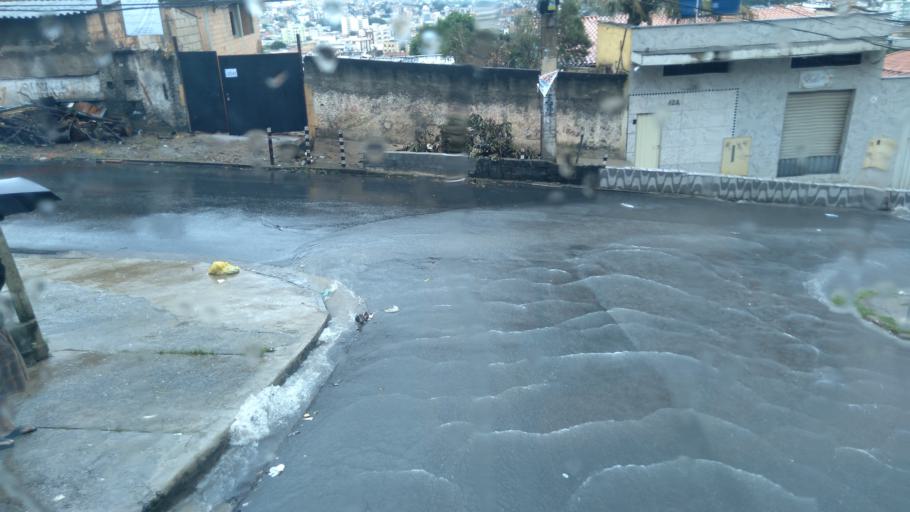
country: BR
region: Minas Gerais
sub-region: Belo Horizonte
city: Belo Horizonte
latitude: -19.9298
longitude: -43.9094
